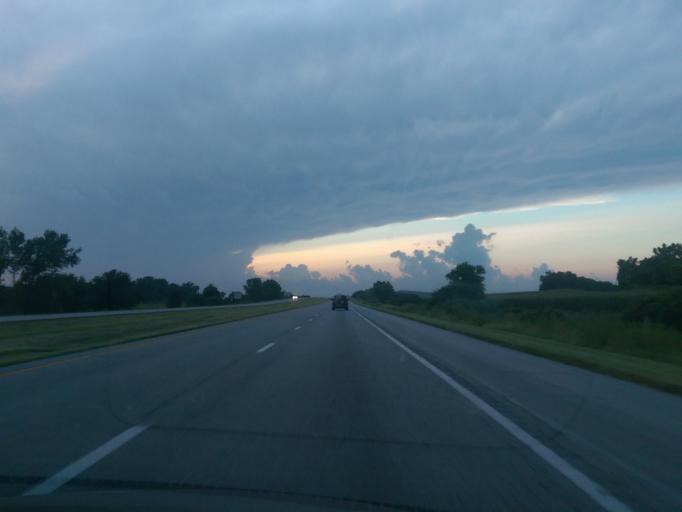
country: US
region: Iowa
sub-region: Fremont County
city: Hamburg
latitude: 40.5631
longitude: -95.6372
